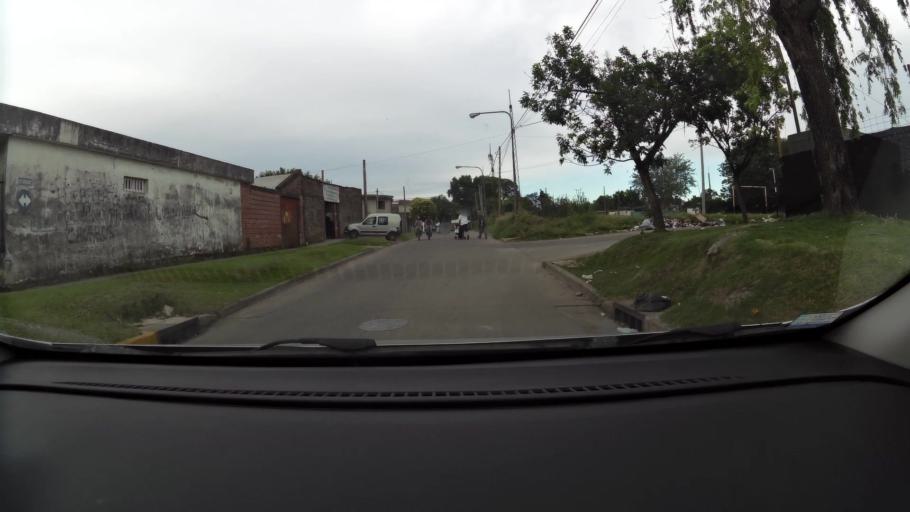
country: AR
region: Santa Fe
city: Granadero Baigorria
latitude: -32.9111
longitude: -60.6920
